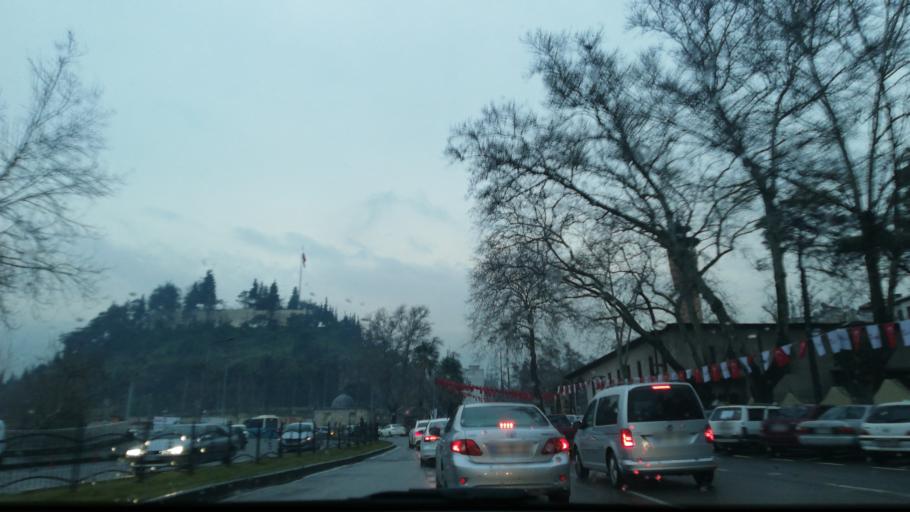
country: TR
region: Kahramanmaras
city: Kahramanmaras
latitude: 37.5839
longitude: 36.9267
